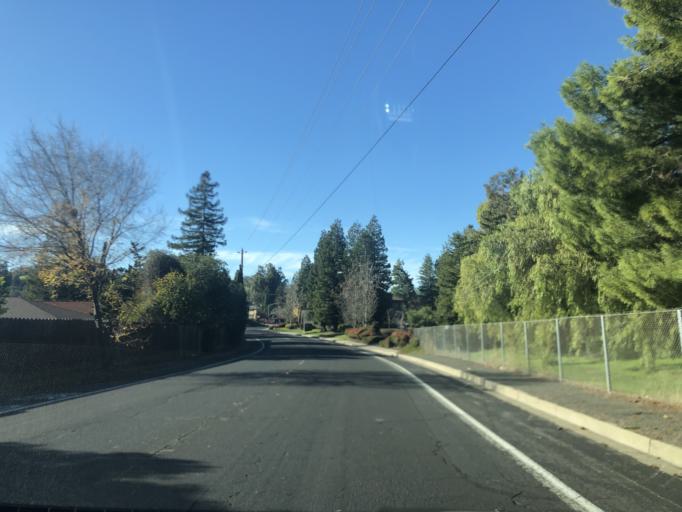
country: US
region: California
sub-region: Contra Costa County
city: Vine Hill
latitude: 37.9904
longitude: -122.0978
